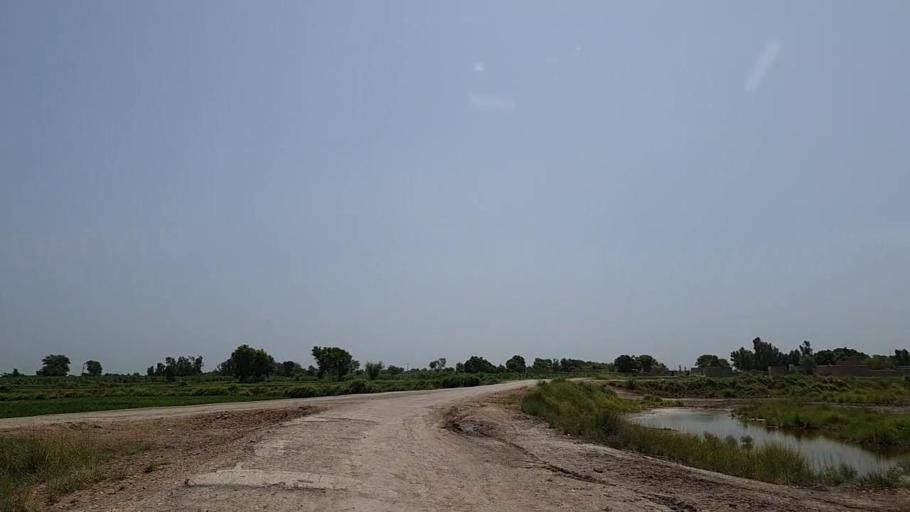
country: PK
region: Sindh
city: Naushahro Firoz
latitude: 26.8436
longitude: 67.9933
